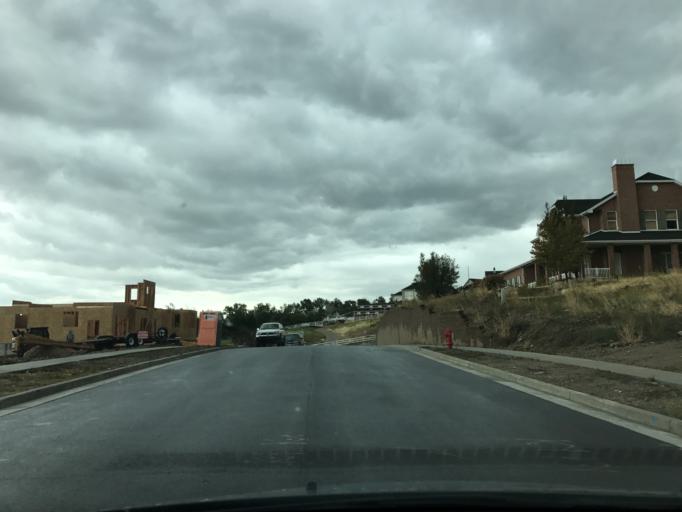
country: US
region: Utah
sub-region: Davis County
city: Fruit Heights
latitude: 41.0074
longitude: -111.8966
